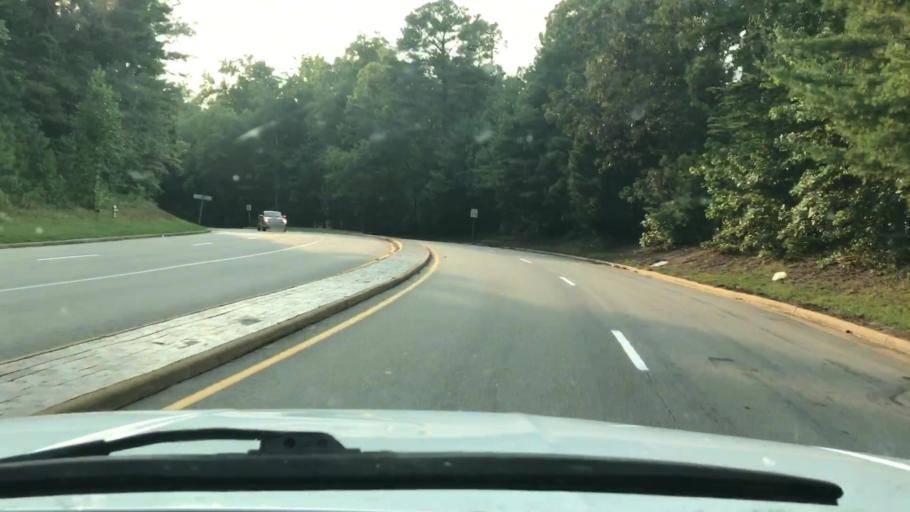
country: US
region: Virginia
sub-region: Chesterfield County
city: Chesterfield
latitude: 37.4110
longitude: -77.5543
